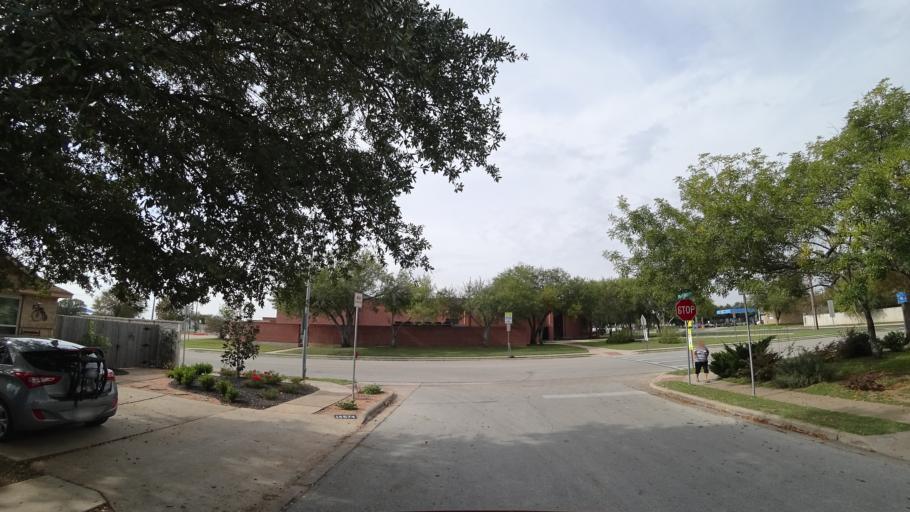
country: US
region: Texas
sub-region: Travis County
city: Wells Branch
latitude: 30.4445
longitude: -97.6854
